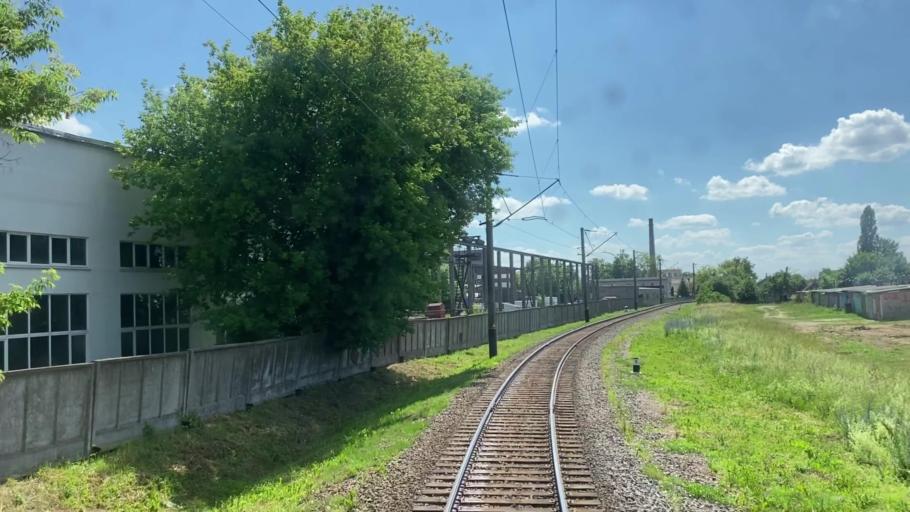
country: BY
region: Brest
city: Baranovichi
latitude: 53.1459
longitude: 26.0309
